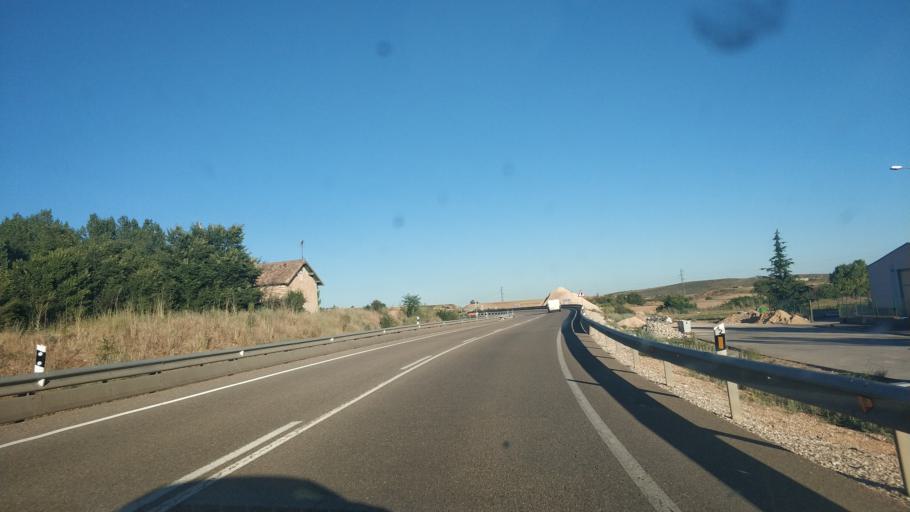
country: ES
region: Castille and Leon
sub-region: Provincia de Soria
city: San Esteban de Gormaz
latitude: 41.5664
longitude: -3.1869
